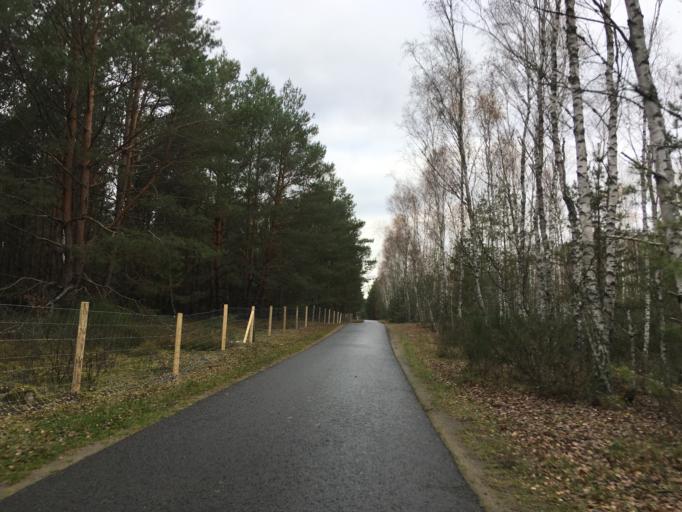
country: DE
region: Brandenburg
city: Jamlitz
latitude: 52.0156
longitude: 14.4864
